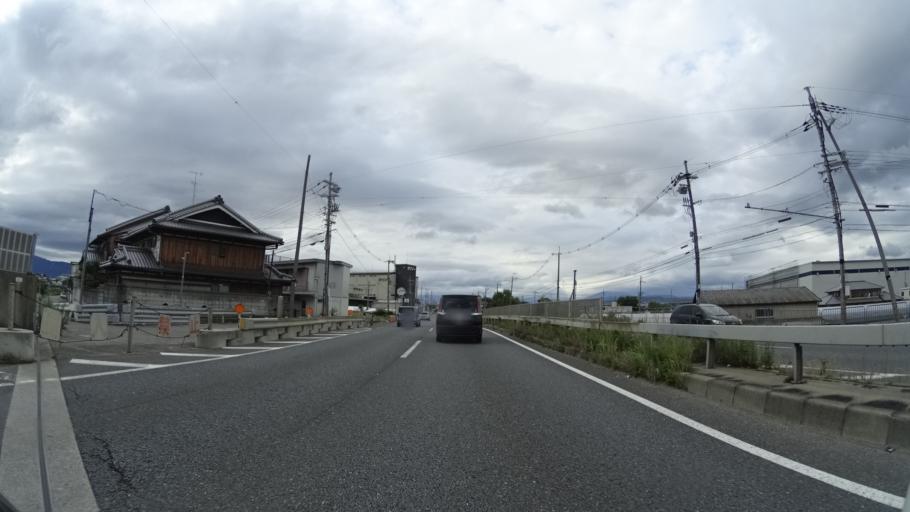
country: JP
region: Kyoto
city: Yawata
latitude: 34.9002
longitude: 135.7441
